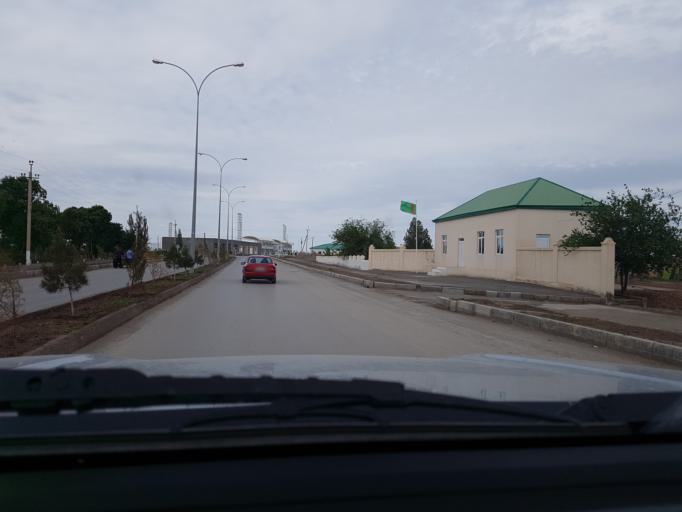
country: TM
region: Lebap
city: Sayat
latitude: 38.4881
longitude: 64.1429
